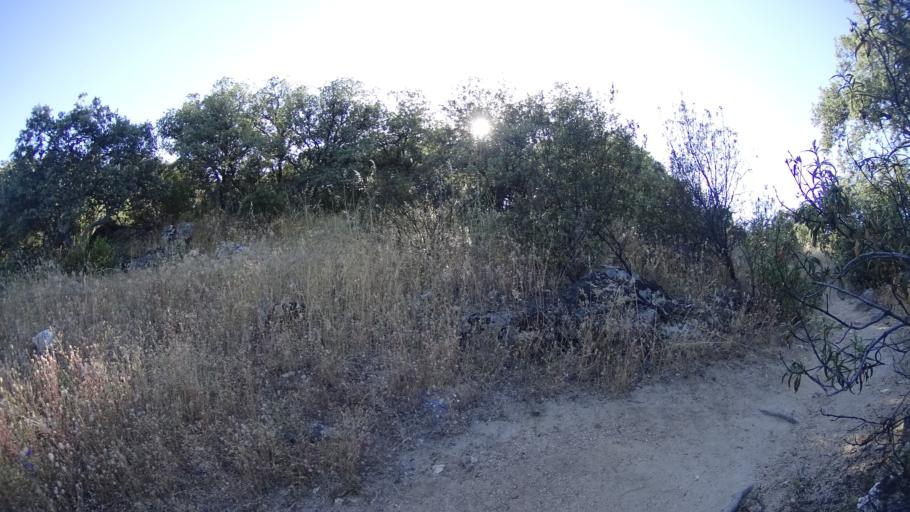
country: ES
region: Madrid
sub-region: Provincia de Madrid
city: Galapagar
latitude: 40.5882
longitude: -3.9737
